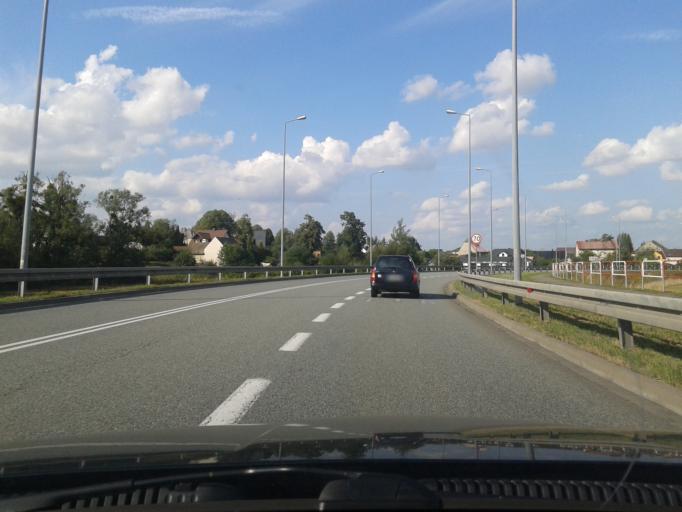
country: PL
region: Silesian Voivodeship
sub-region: Powiat raciborski
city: Chalupki
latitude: 49.9194
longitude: 18.3195
